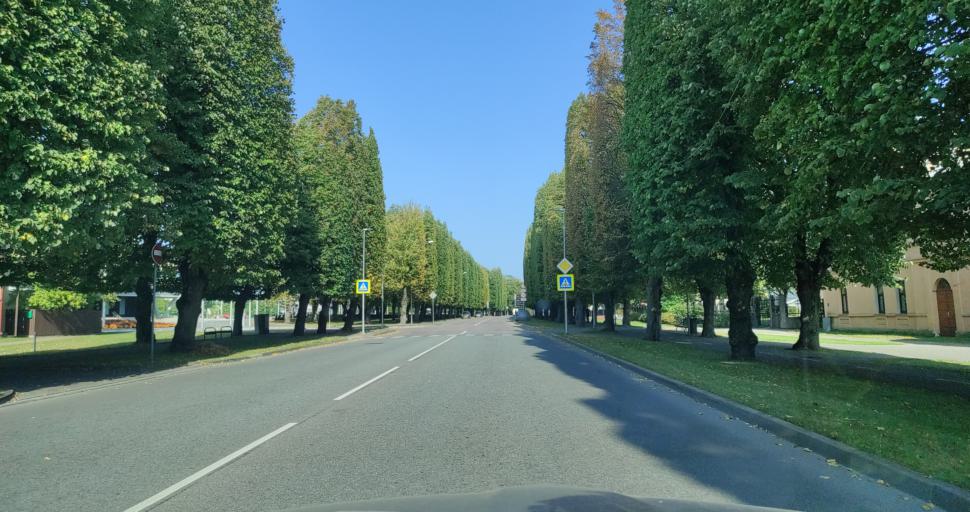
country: LV
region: Ventspils
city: Ventspils
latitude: 57.3868
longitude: 21.5657
